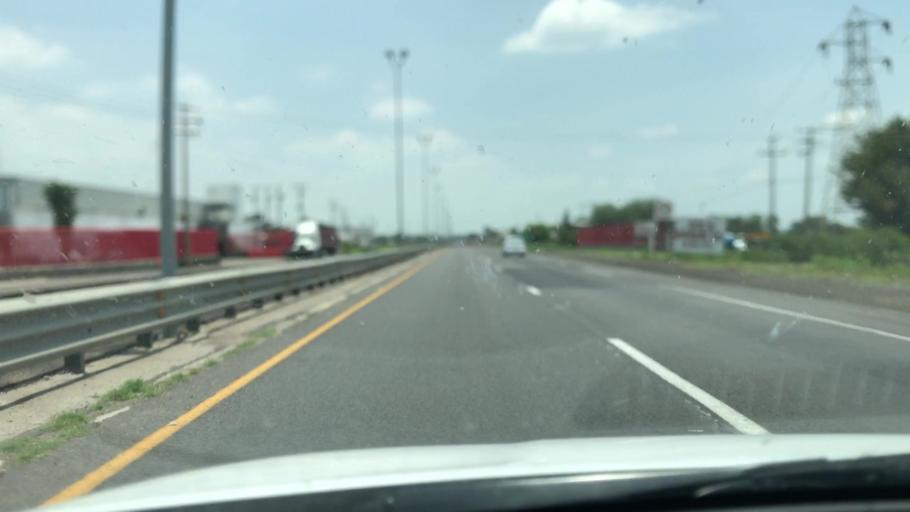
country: MX
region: Guanajuato
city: Penjamo
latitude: 20.4282
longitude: -101.7072
